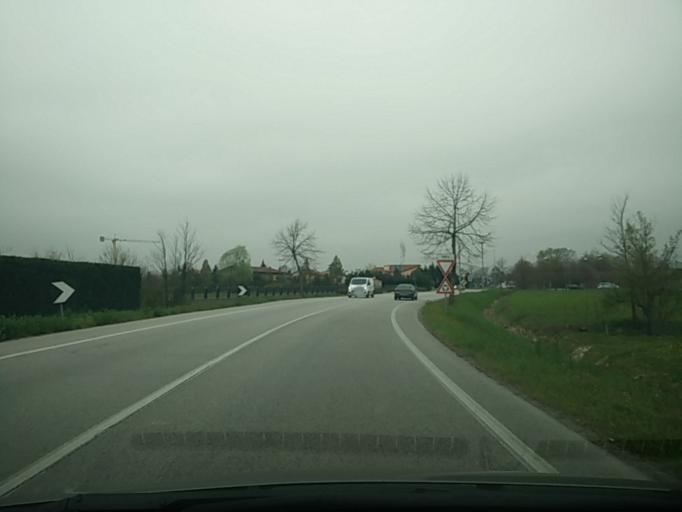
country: IT
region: Veneto
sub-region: Provincia di Venezia
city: Mirano
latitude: 45.4818
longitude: 12.1101
